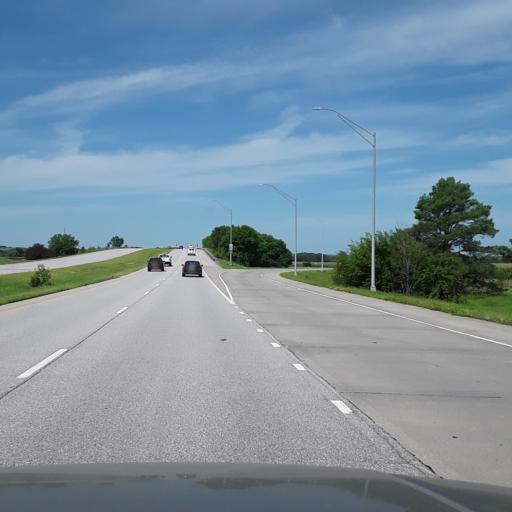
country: US
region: Nebraska
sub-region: Lancaster County
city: Lincoln
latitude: 40.8795
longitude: -96.7541
